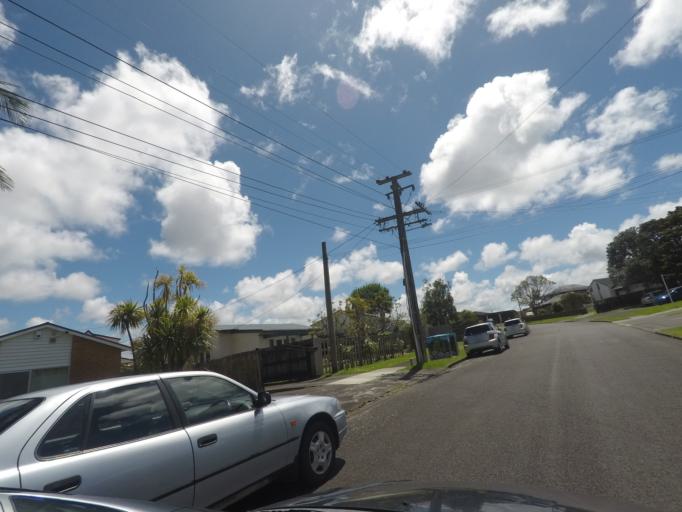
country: NZ
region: Auckland
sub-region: Auckland
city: Rosebank
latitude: -36.8805
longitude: 174.6432
